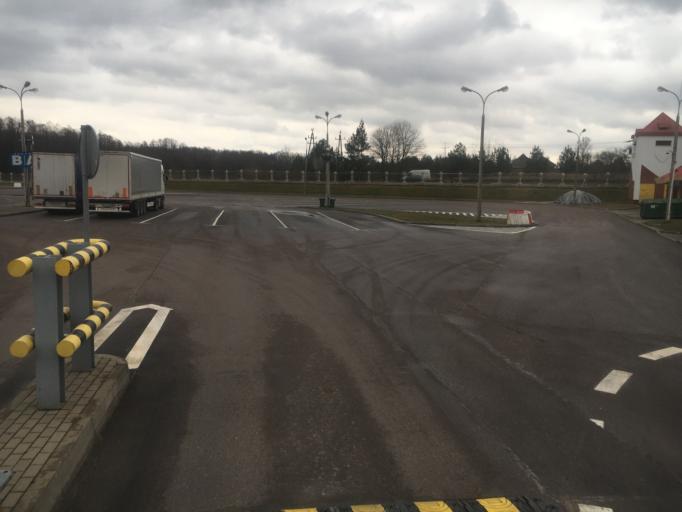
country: BY
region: Grodnenskaya
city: Vyalikaya Byerastavitsa
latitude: 53.1232
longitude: 23.8892
